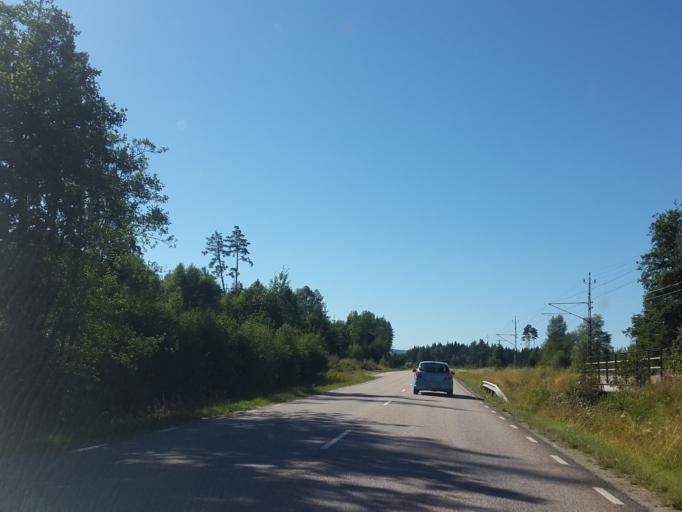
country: SE
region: Vaestra Goetaland
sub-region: Boras Kommun
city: Boras
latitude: 57.8503
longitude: 13.0125
